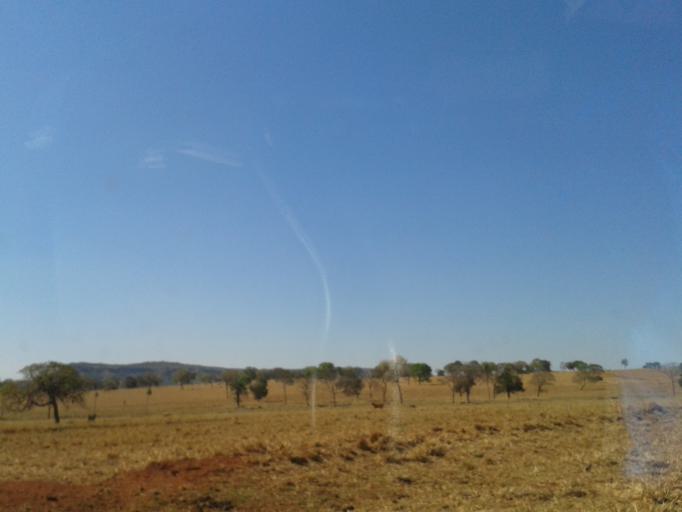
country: BR
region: Minas Gerais
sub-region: Santa Vitoria
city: Santa Vitoria
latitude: -19.0852
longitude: -50.0675
